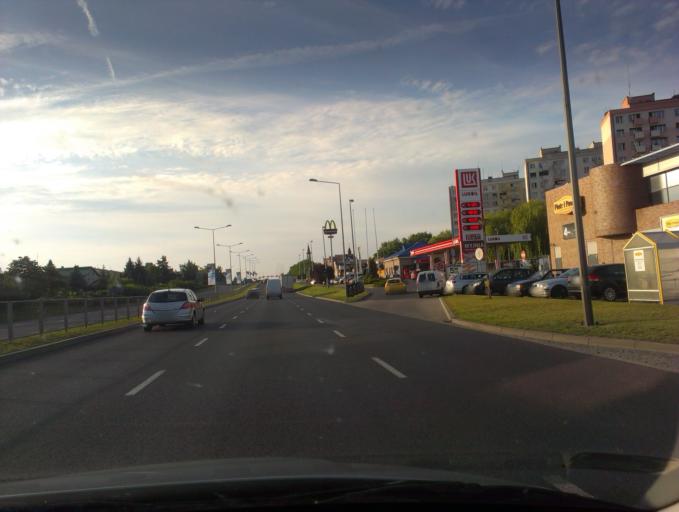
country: PL
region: Greater Poland Voivodeship
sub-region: Leszno
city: Leszno
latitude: 51.8427
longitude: 16.5935
